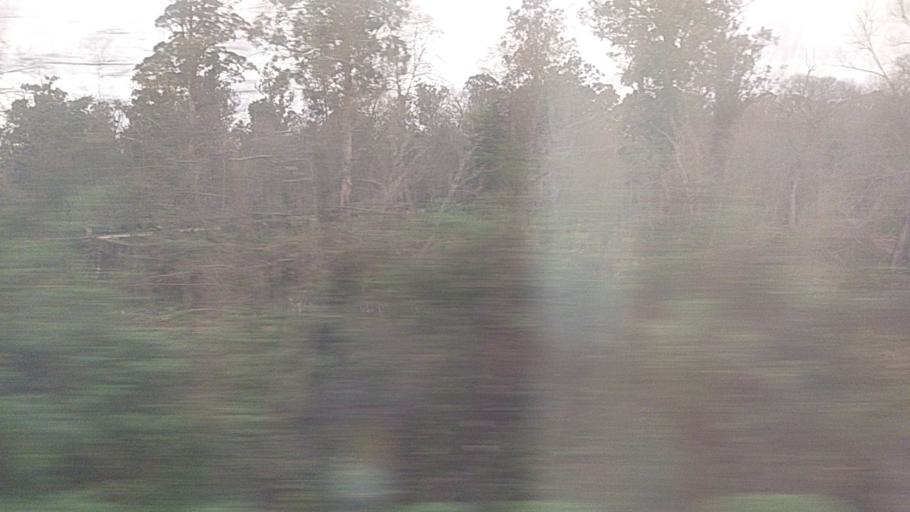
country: PT
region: Coimbra
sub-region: Coimbra
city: Coimbra
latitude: 40.2194
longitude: -8.4419
